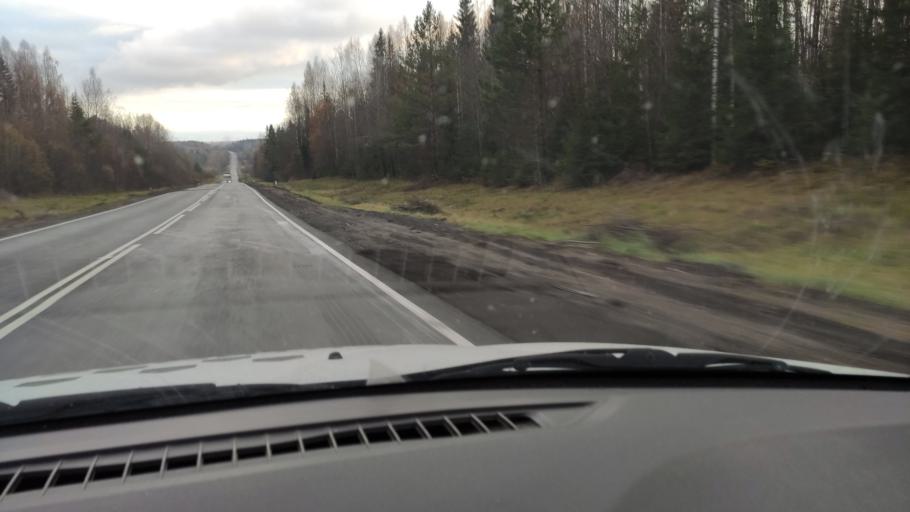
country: RU
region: Kirov
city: Omutninsk
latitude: 58.7359
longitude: 52.0720
